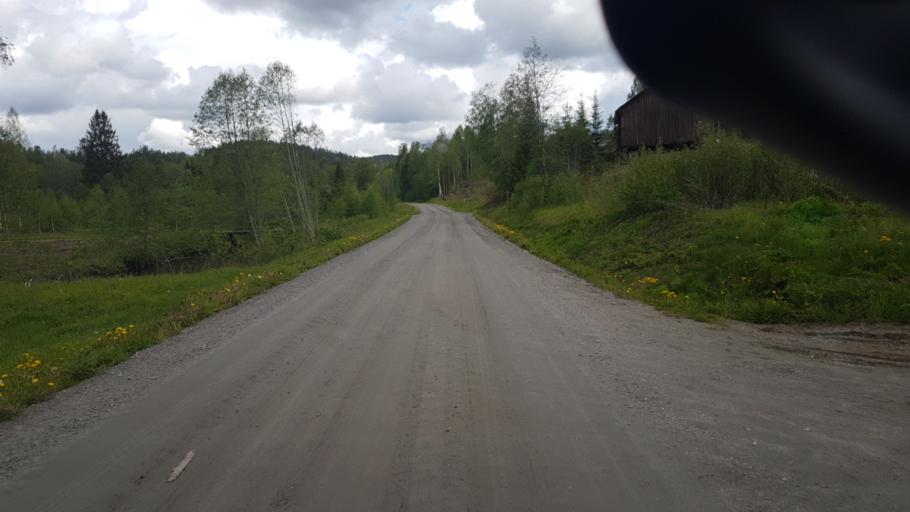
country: NO
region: Ostfold
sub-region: Romskog
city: Romskog
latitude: 59.6778
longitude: 11.9336
